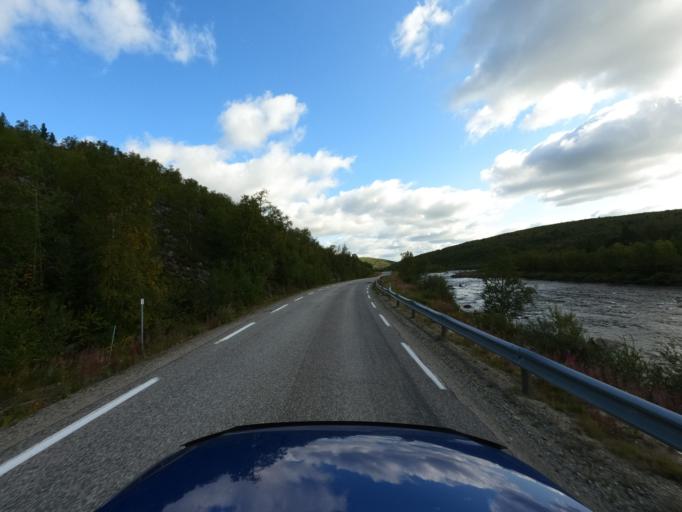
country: NO
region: Finnmark Fylke
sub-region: Porsanger
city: Lakselv
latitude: 69.4270
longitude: 24.8660
